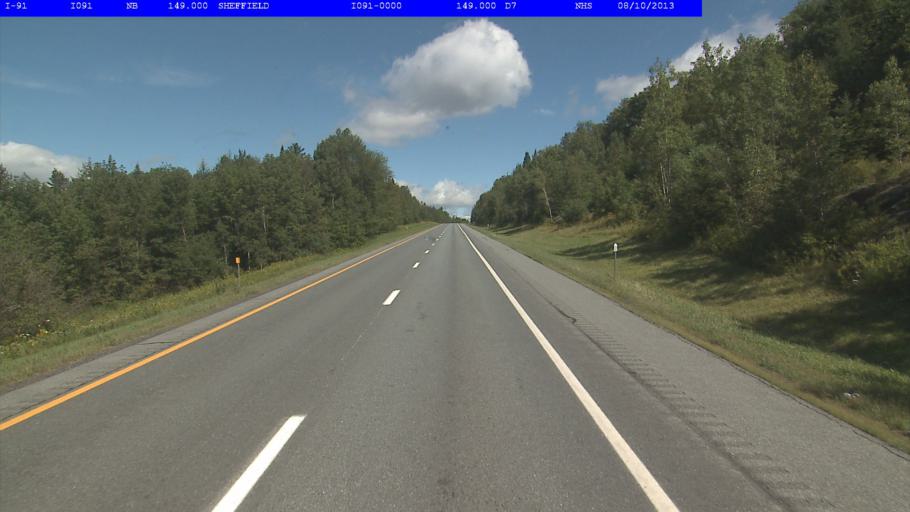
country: US
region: Vermont
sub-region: Caledonia County
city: Lyndonville
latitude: 44.6502
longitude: -72.1326
